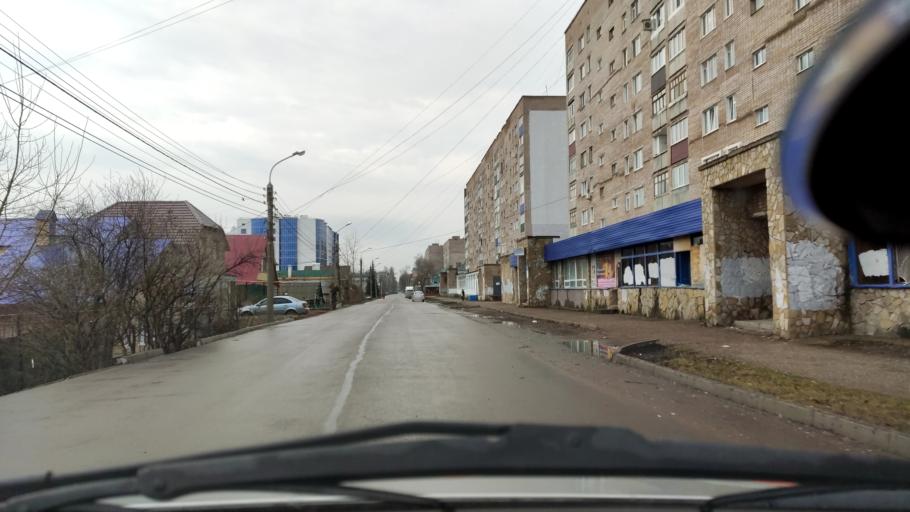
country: RU
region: Bashkortostan
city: Sterlitamak
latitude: 53.6239
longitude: 55.9565
